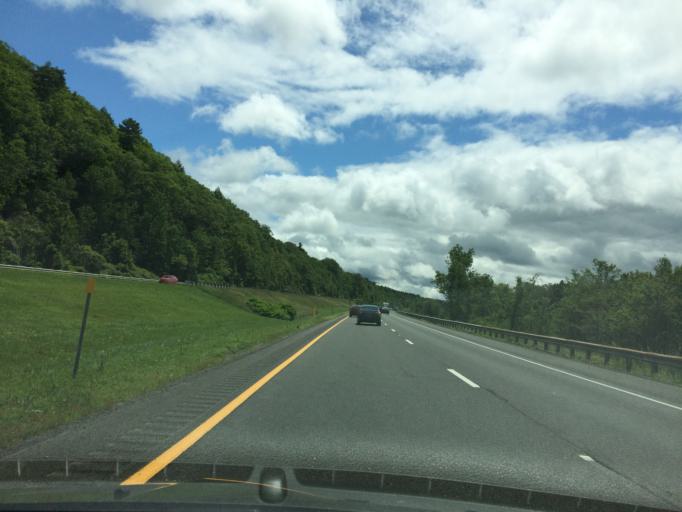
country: US
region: Massachusetts
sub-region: Berkshire County
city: Becket
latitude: 42.2753
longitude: -73.1391
